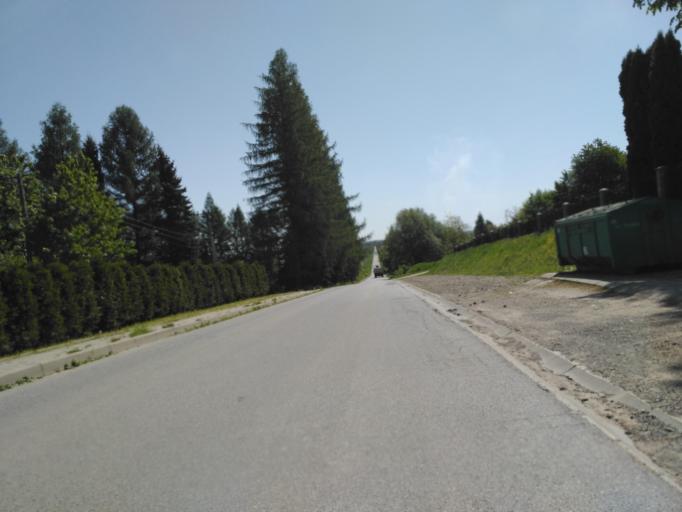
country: PL
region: Subcarpathian Voivodeship
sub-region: Powiat krosnienski
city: Miejsce Piastowe
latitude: 49.6117
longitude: 21.7588
